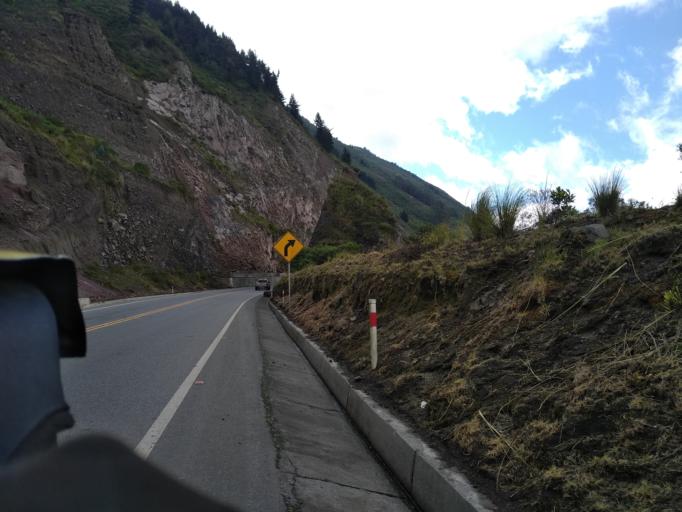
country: EC
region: Tungurahua
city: Banos
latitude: -1.4853
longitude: -78.5181
